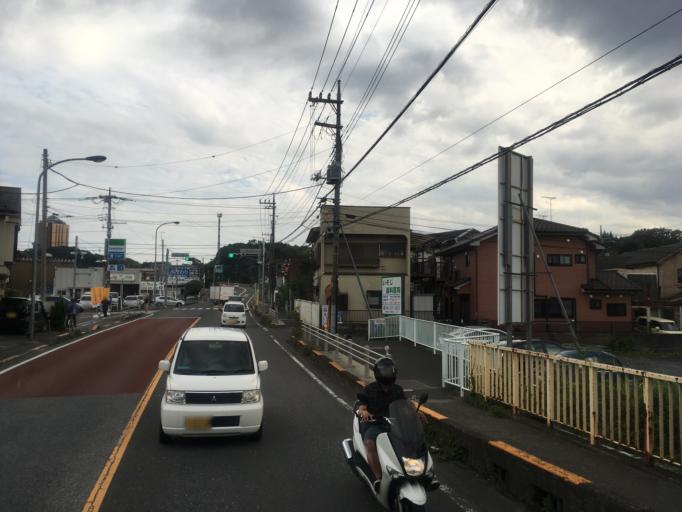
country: JP
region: Tokyo
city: Hachioji
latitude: 35.6365
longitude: 139.3393
